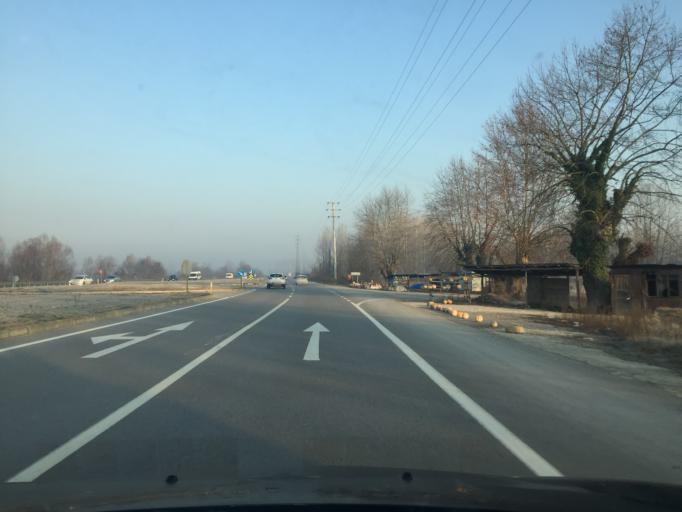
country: TR
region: Sakarya
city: Akyazi
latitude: 40.6870
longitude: 30.5754
